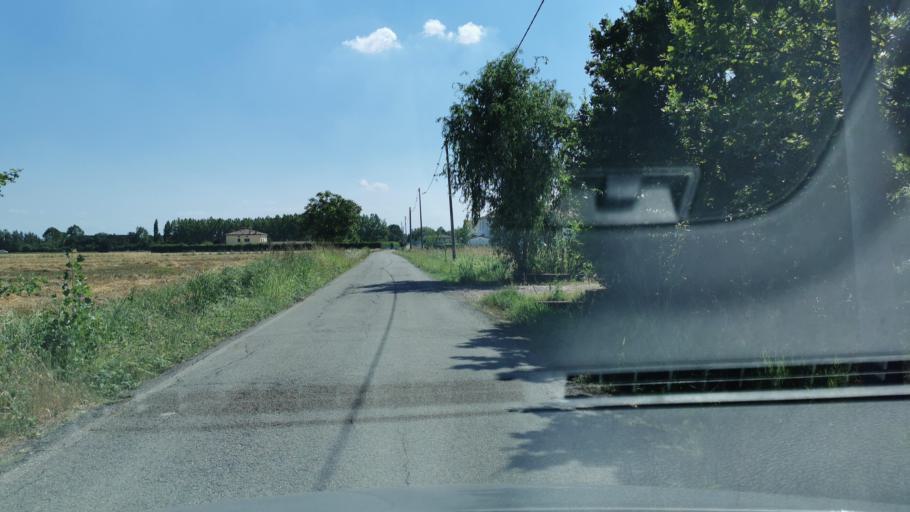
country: IT
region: Emilia-Romagna
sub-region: Provincia di Modena
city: Fossoli
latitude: 44.8088
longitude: 10.8970
